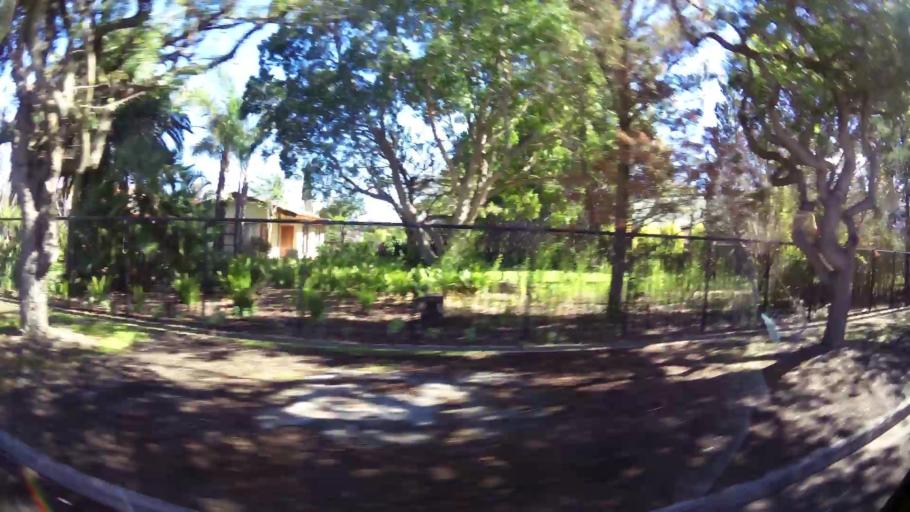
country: ZA
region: Western Cape
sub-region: Cape Winelands District Municipality
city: Ashton
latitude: -33.8070
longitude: 19.8977
